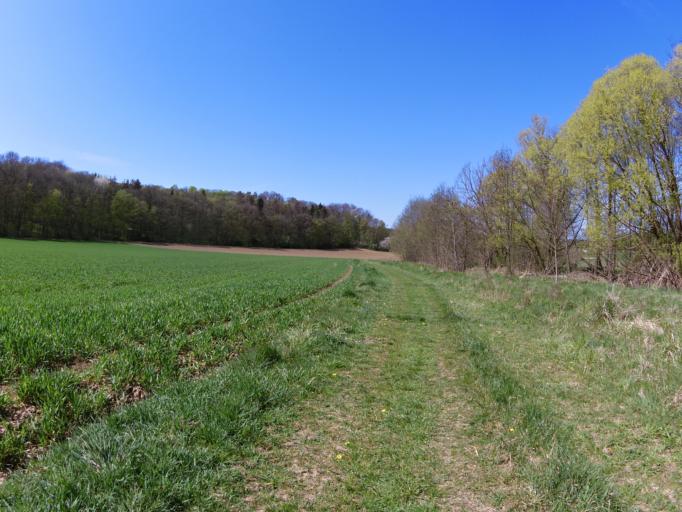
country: DE
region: Bavaria
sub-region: Regierungsbezirk Unterfranken
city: Estenfeld
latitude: 49.8566
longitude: 10.0022
